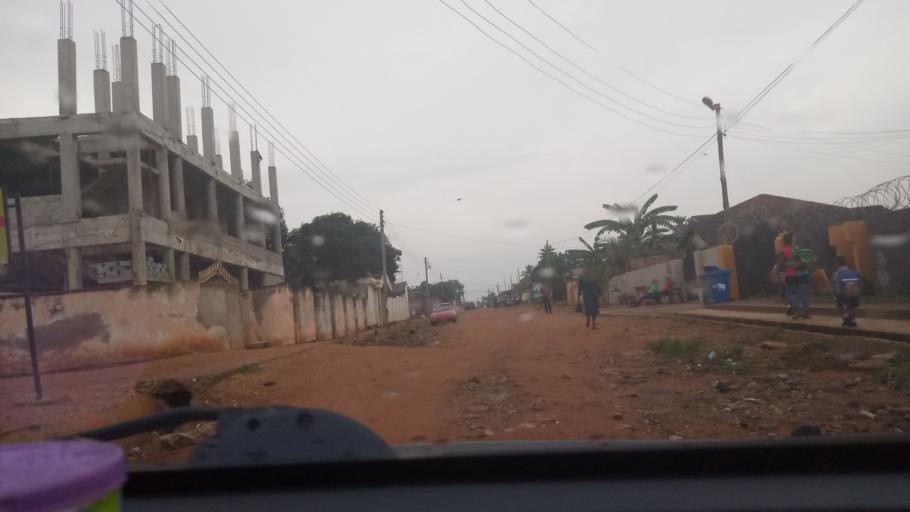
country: GH
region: Greater Accra
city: Medina Estates
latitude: 5.7028
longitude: -0.1662
